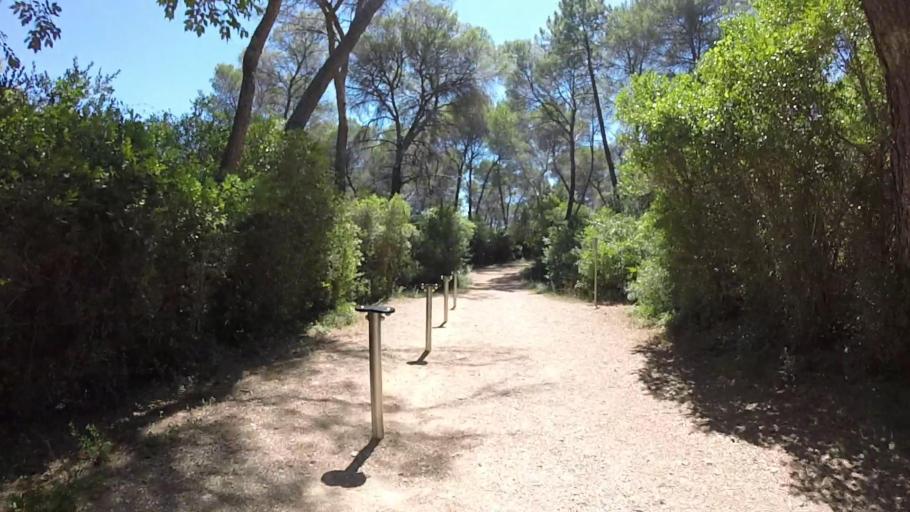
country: FR
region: Provence-Alpes-Cote d'Azur
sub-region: Departement des Alpes-Maritimes
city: Vallauris
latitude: 43.6089
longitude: 7.0404
